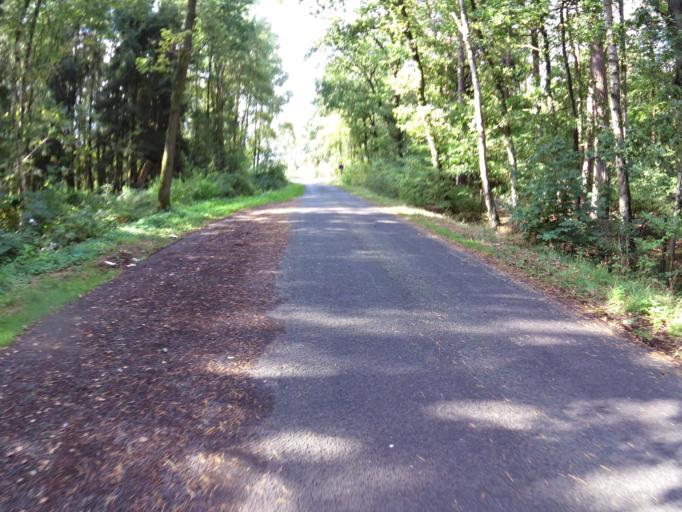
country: DE
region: Lower Saxony
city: Bremervorde
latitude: 53.4675
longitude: 9.1419
